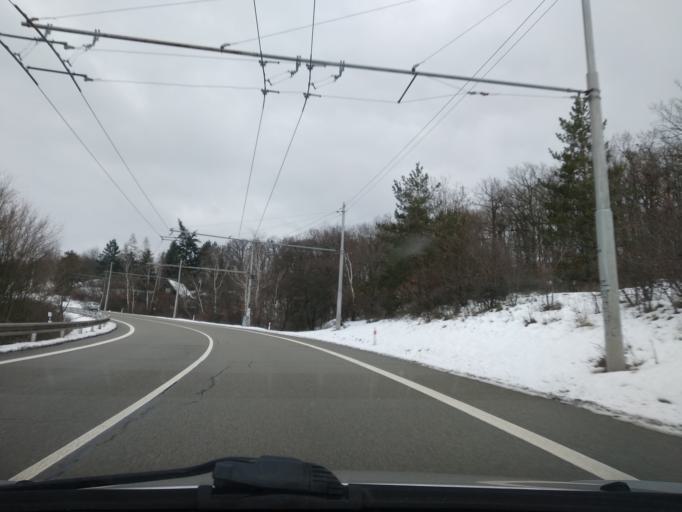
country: CZ
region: South Moravian
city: Ostopovice
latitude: 49.1833
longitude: 16.5445
